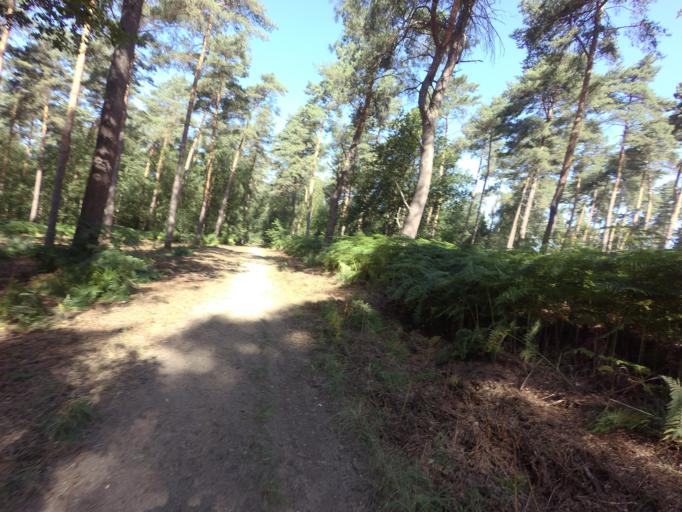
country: DE
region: North Rhine-Westphalia
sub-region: Regierungsbezirk Koln
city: Wassenberg
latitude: 51.1531
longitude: 6.1342
